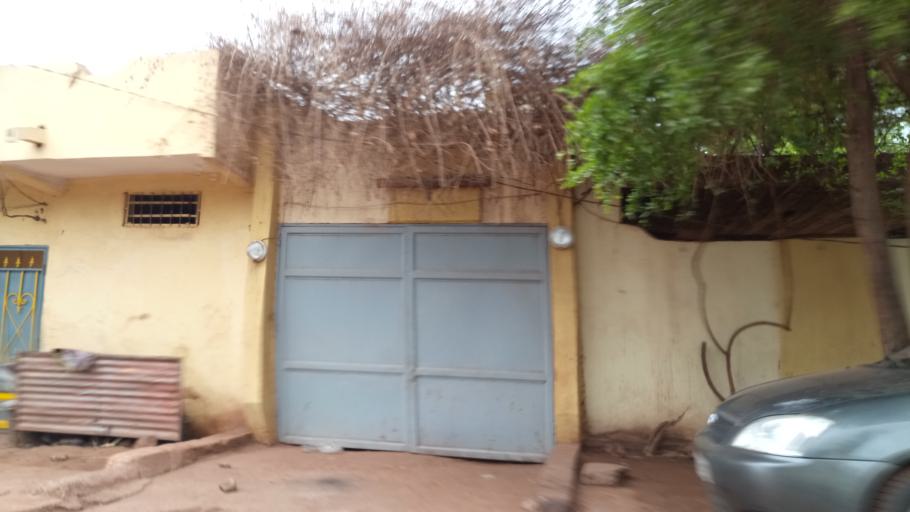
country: ML
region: Bamako
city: Bamako
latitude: 12.5886
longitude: -7.9910
